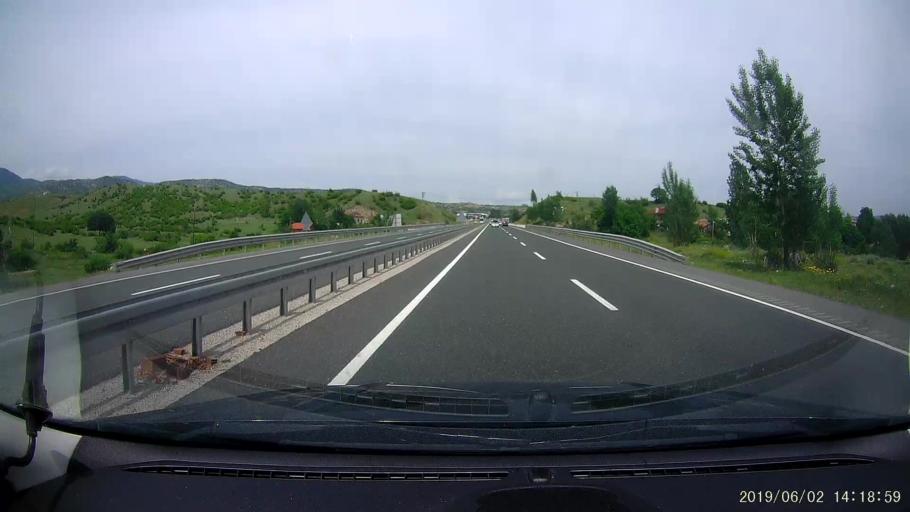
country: TR
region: Kastamonu
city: Tosya
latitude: 40.9592
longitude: 33.9685
